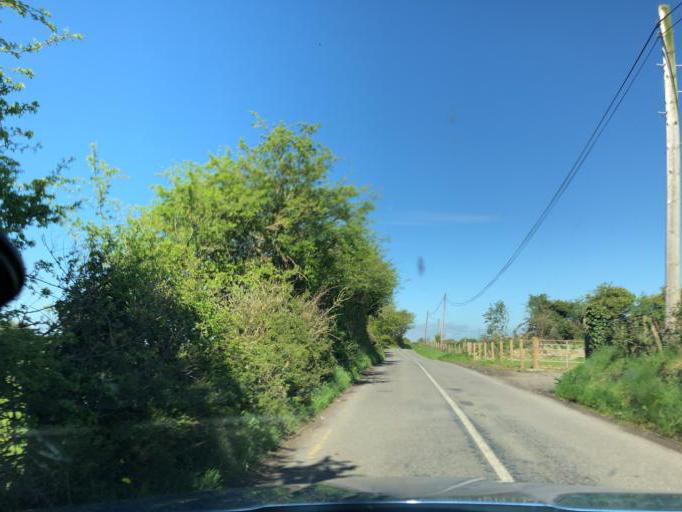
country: IE
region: Connaught
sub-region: County Galway
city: Portumna
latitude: 53.1607
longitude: -8.2721
